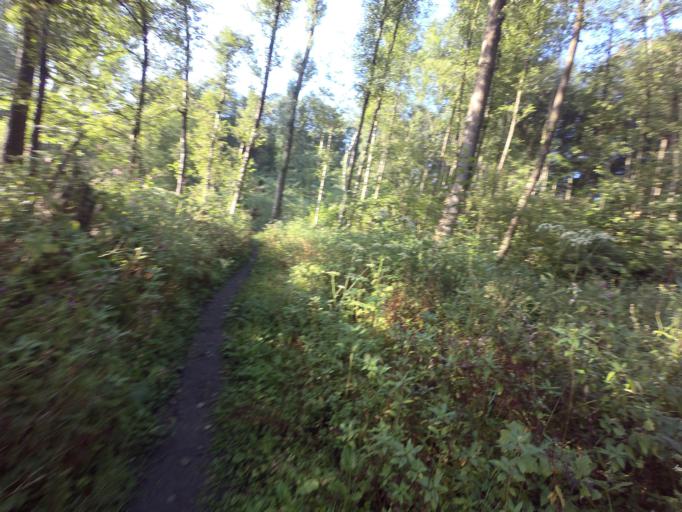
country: DE
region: North Rhine-Westphalia
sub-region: Regierungsbezirk Koln
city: Herzogenrath
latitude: 50.8450
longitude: 6.0921
